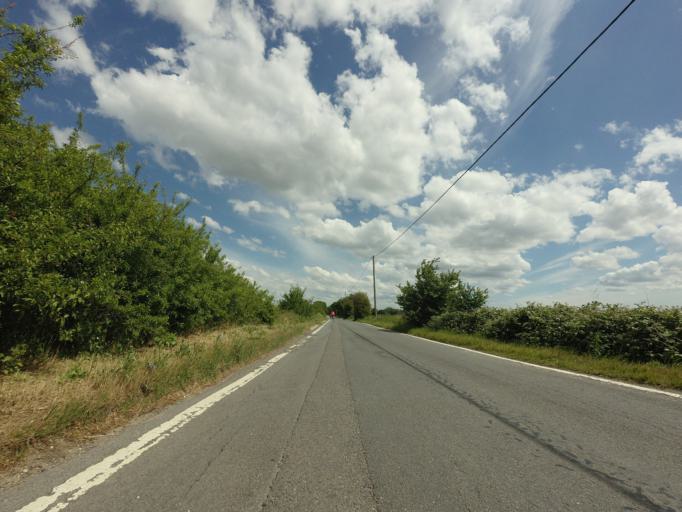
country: GB
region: England
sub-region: Medway
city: High Halstow
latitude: 51.4460
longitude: 0.5712
